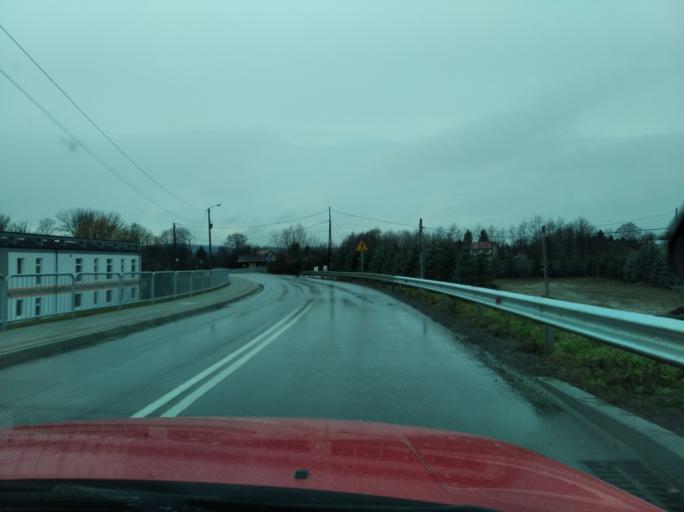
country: PL
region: Subcarpathian Voivodeship
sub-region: Powiat rzeszowski
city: Siedliska
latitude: 49.9507
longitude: 21.9326
